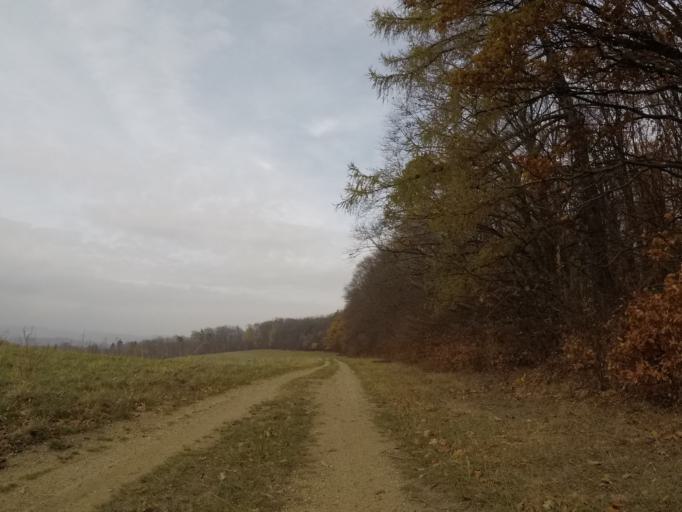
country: SK
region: Presovsky
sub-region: Okres Presov
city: Presov
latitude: 48.9332
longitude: 21.1291
